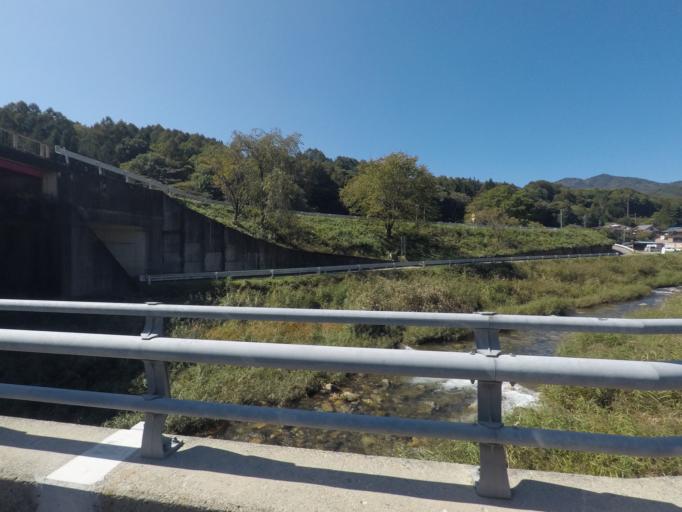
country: JP
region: Nagano
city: Tatsuno
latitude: 35.9766
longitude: 137.7495
